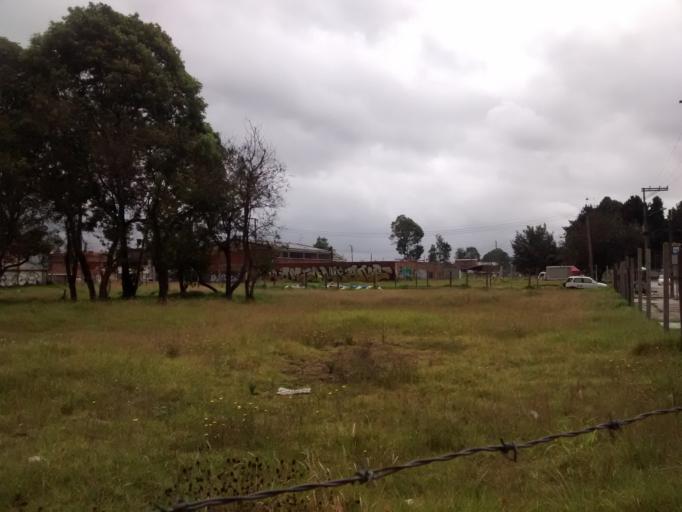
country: CO
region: Bogota D.C.
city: Bogota
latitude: 4.6809
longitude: -74.1277
